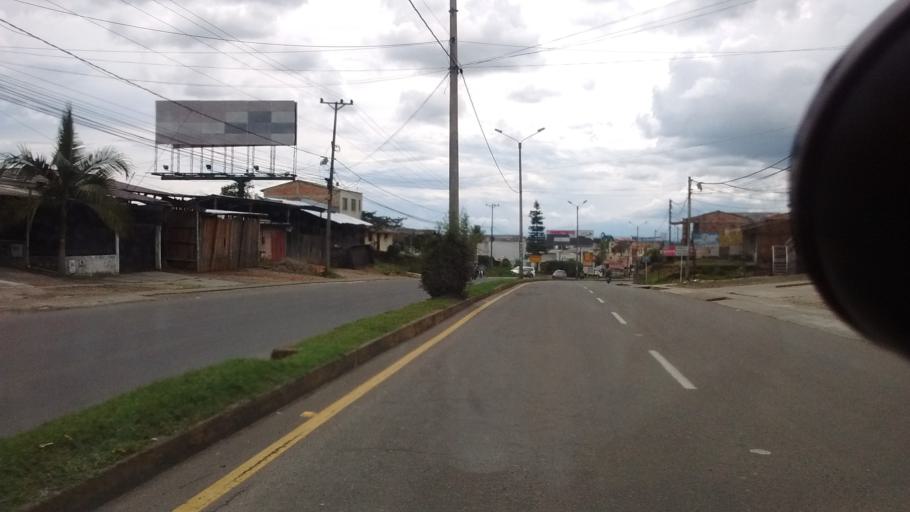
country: CO
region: Cauca
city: Popayan
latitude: 2.4813
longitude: -76.5662
